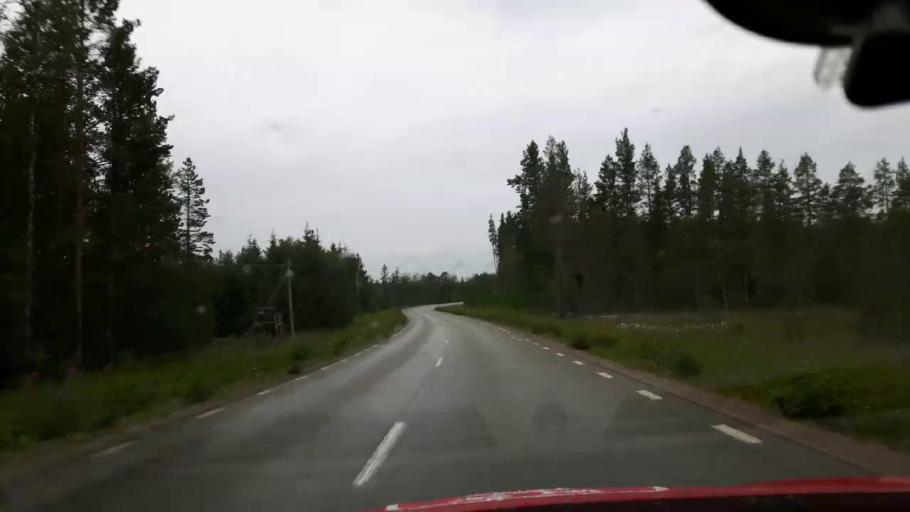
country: SE
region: Jaemtland
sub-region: OEstersunds Kommun
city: Brunflo
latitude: 62.8220
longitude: 14.9990
